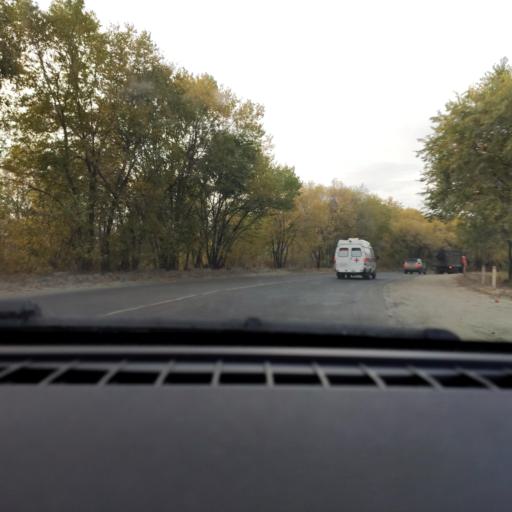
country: RU
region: Voronezj
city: Maslovka
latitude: 51.6209
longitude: 39.2345
